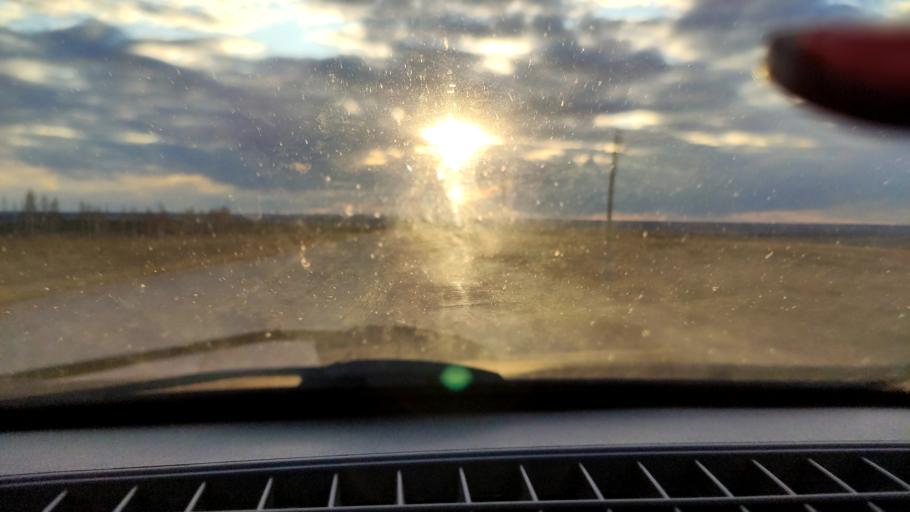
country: RU
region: Bashkortostan
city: Tolbazy
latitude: 54.0110
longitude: 55.5782
